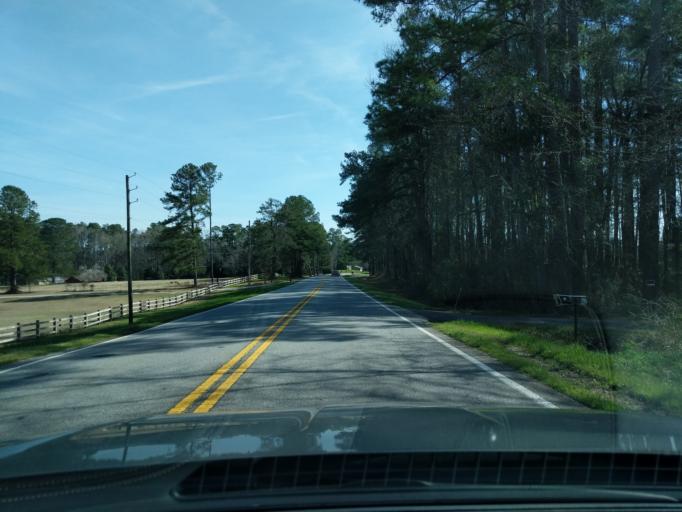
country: US
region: Georgia
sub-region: Columbia County
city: Evans
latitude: 33.5323
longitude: -82.1427
